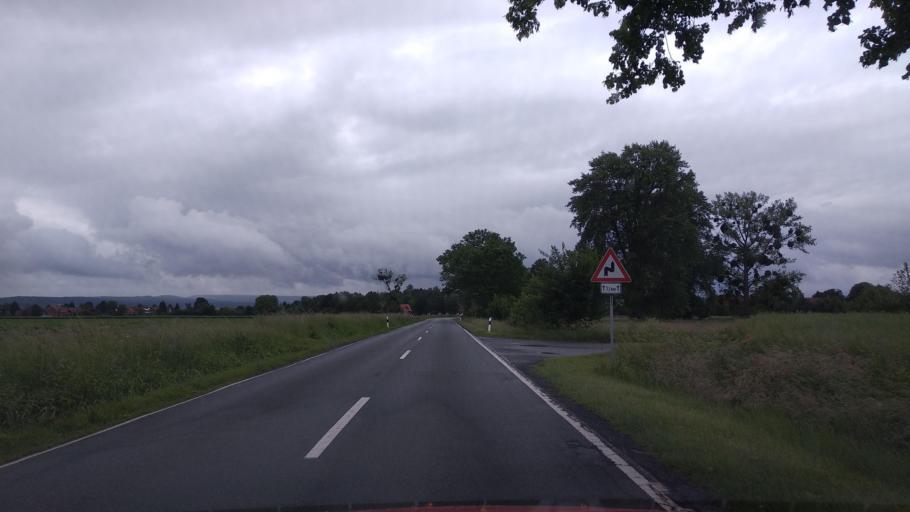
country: DE
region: Lower Saxony
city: Ludersfeld
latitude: 52.3679
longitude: 9.2563
